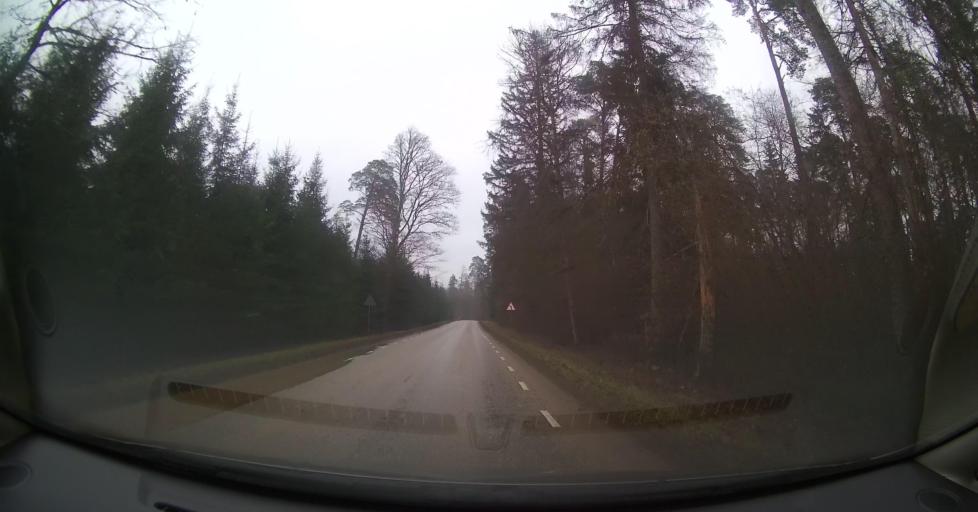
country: EE
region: Tartu
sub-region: UElenurme vald
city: Ulenurme
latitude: 58.3434
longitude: 26.8317
